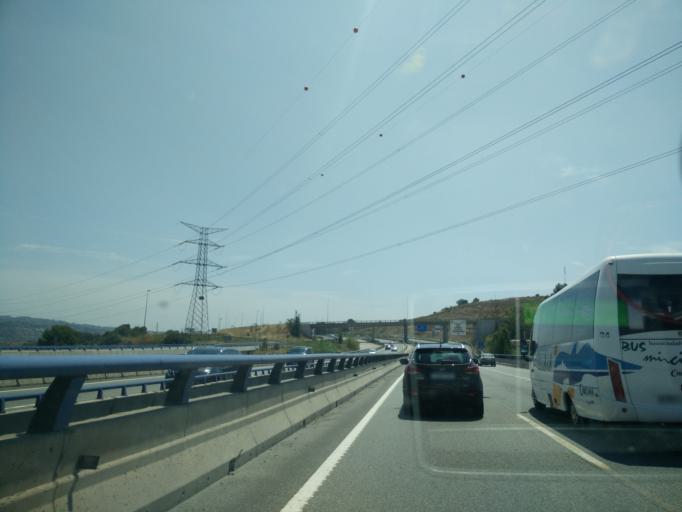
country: ES
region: Catalonia
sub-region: Provincia de Barcelona
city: Esparreguera
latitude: 41.5245
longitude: 1.8833
